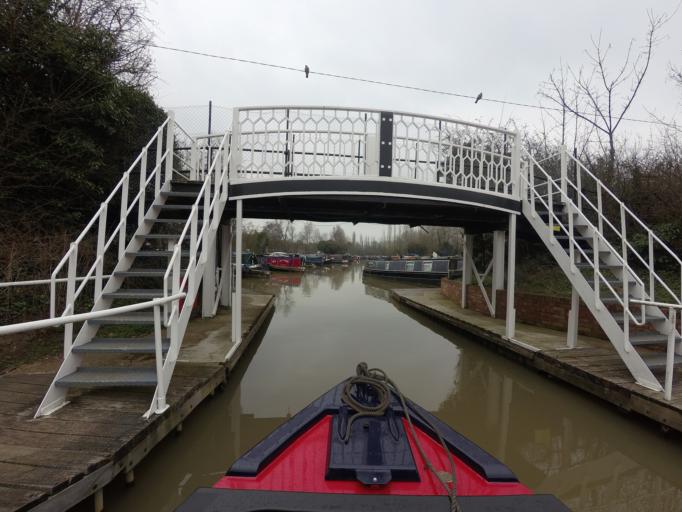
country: GB
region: England
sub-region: Northamptonshire
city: Daventry
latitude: 52.2882
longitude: -1.2094
